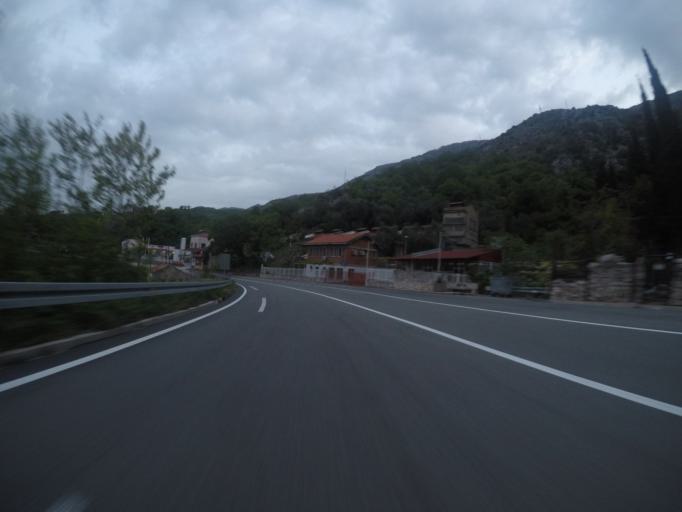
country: ME
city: Petrovac na Moru
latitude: 42.1963
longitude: 18.9828
